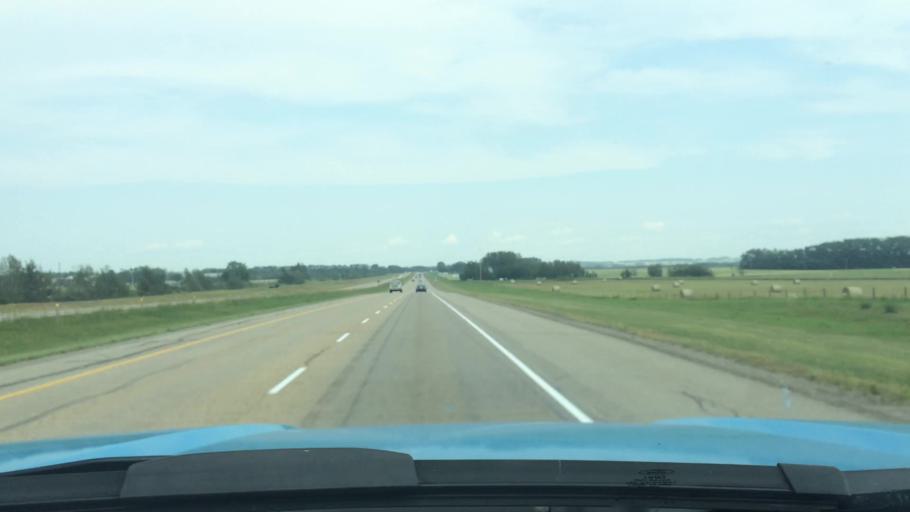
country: CA
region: Alberta
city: Olds
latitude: 51.9662
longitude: -114.0066
